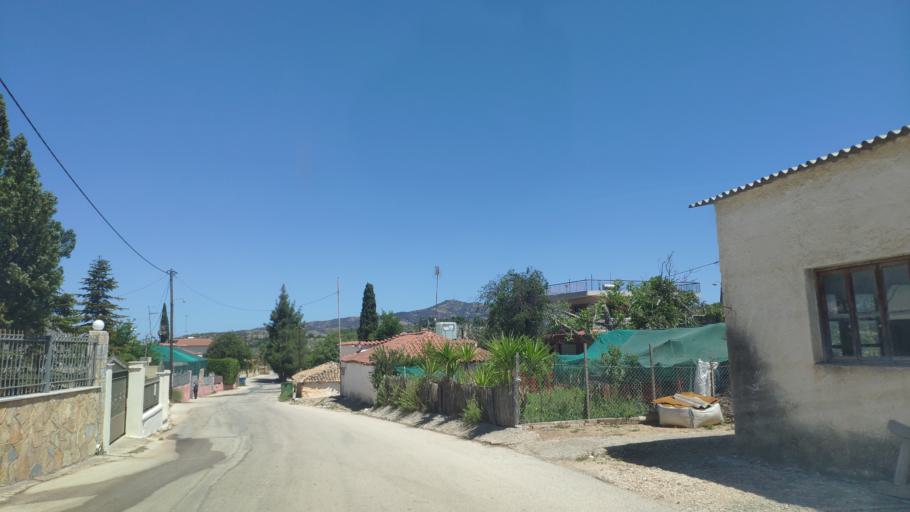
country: GR
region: Peloponnese
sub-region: Nomos Korinthias
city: Athikia
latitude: 37.8179
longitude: 22.9242
